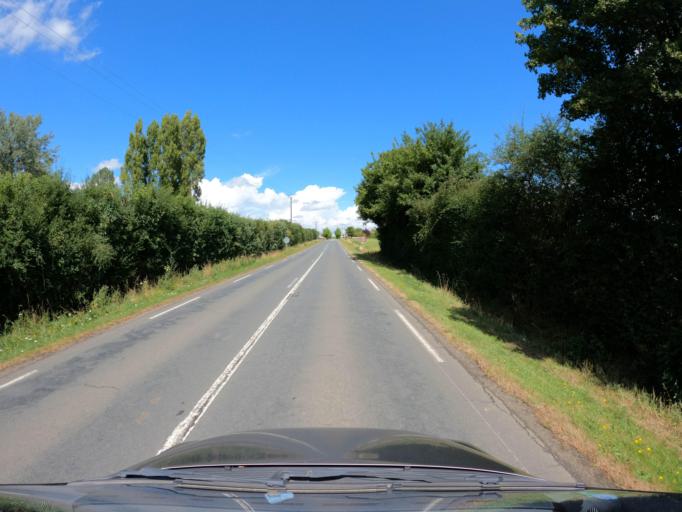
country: FR
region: Pays de la Loire
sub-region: Departement de la Sarthe
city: Juigne-sur-Sarthe
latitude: 47.9151
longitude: -0.2693
